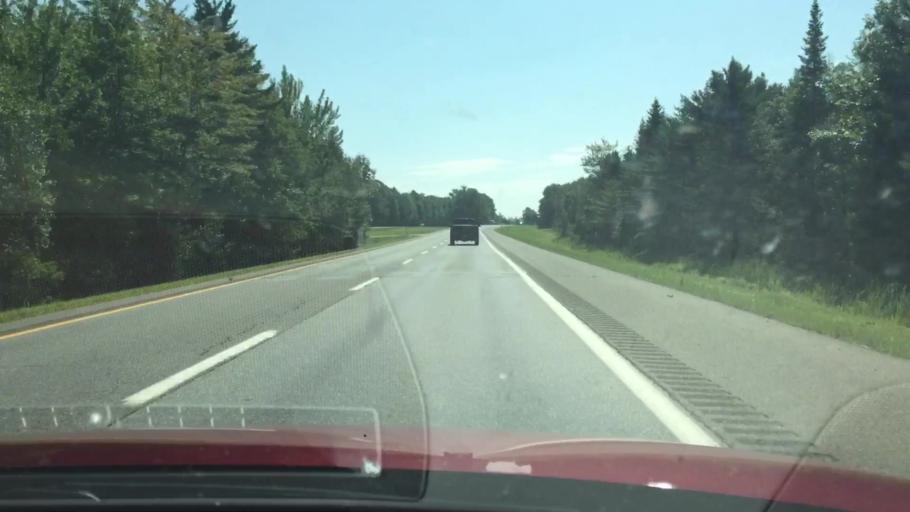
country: US
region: Maine
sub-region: Penobscot County
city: Orono
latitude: 44.8811
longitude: -68.6975
